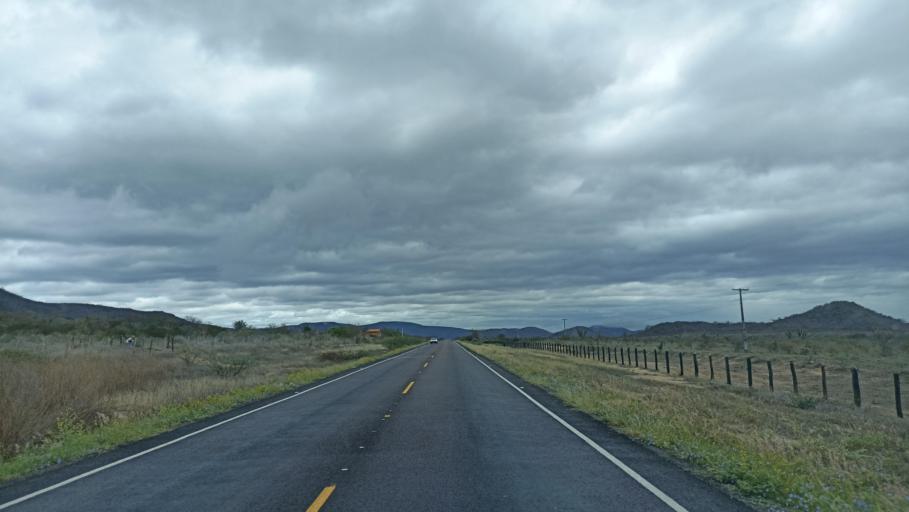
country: BR
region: Bahia
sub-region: Iacu
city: Iacu
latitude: -12.8999
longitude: -40.4018
